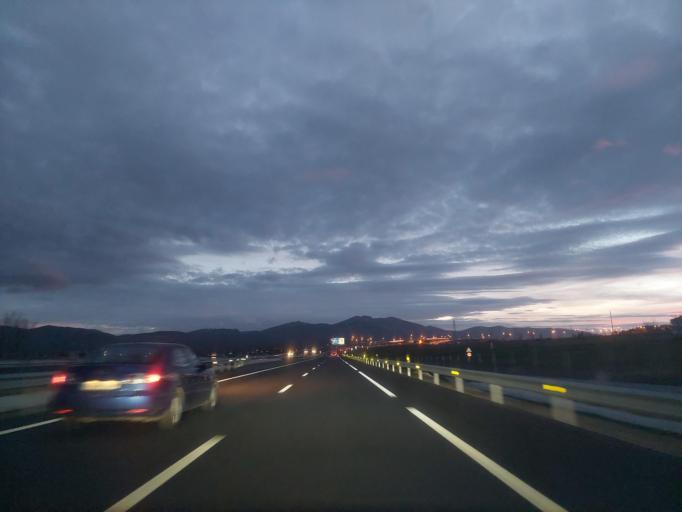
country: ES
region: Castille and Leon
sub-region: Provincia de Segovia
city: San Cristobal de Segovia
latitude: 40.9354
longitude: -4.0861
